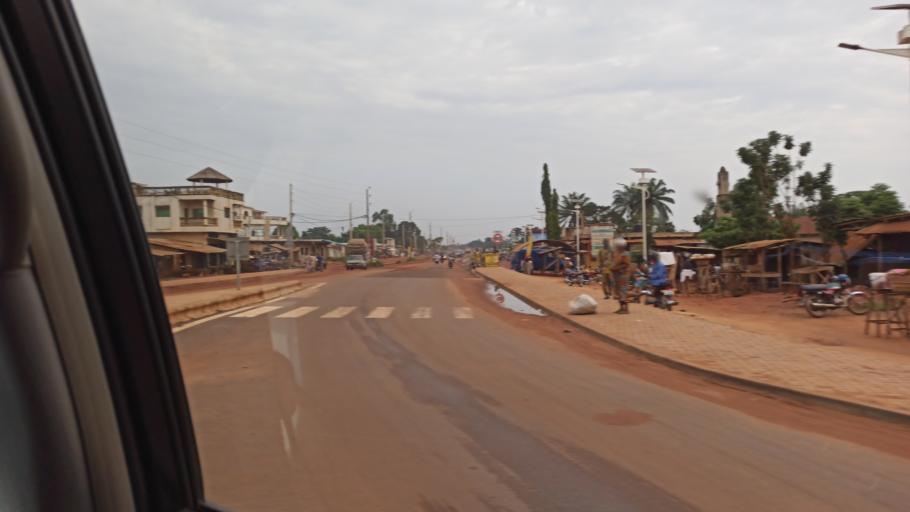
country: BJ
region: Queme
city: Porto-Novo
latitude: 6.5603
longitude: 2.5890
